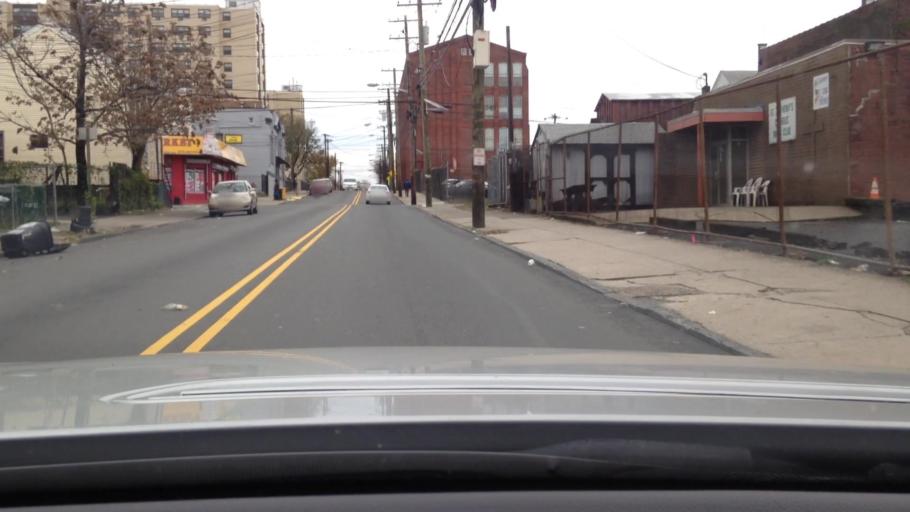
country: US
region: New Jersey
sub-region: Passaic County
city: Paterson
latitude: 40.9091
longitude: -74.1636
